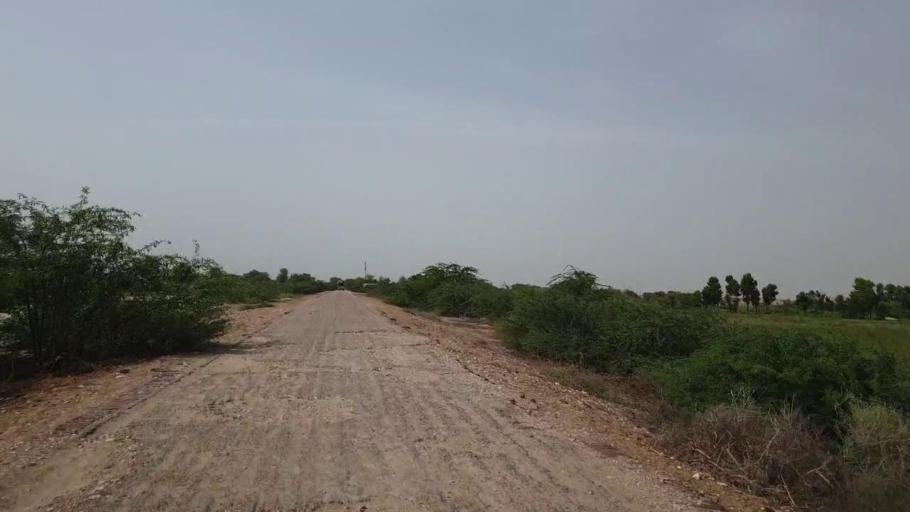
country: PK
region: Sindh
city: Bandhi
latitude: 26.5495
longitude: 68.3844
